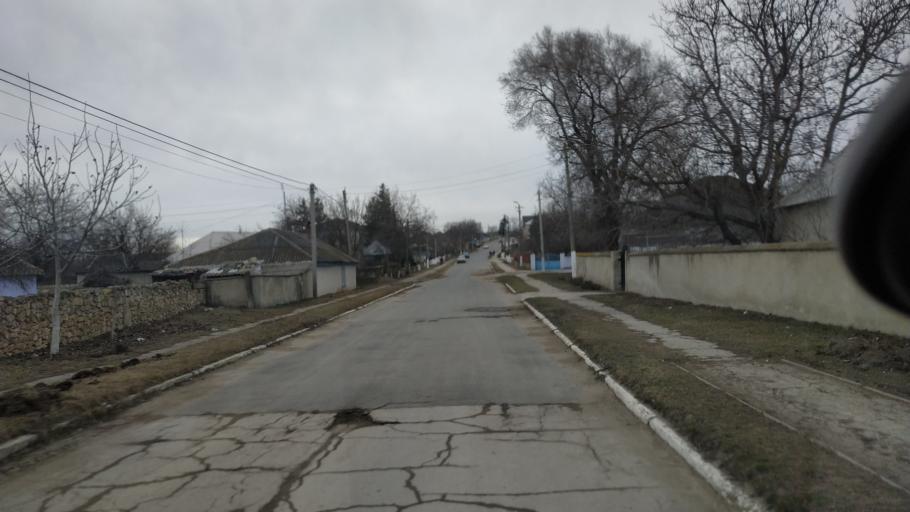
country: MD
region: Telenesti
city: Cocieri
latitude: 47.2586
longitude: 29.0657
